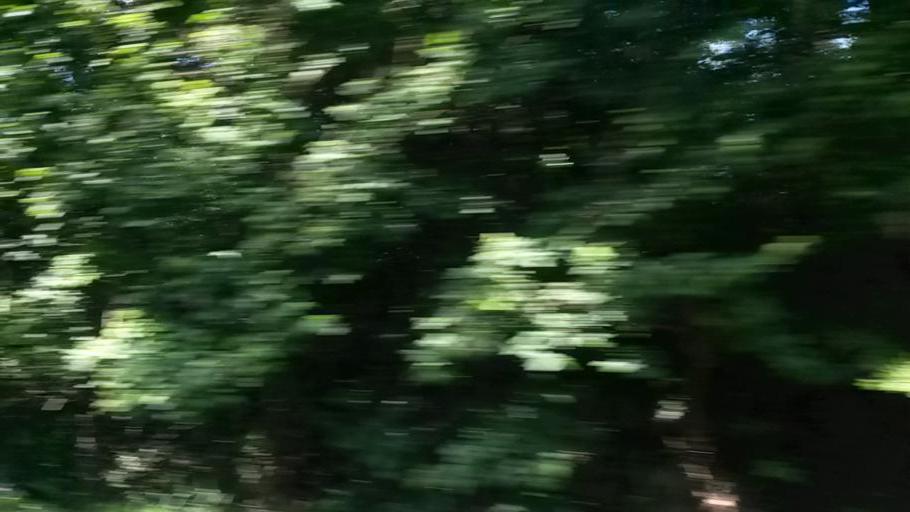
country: IE
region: Leinster
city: Donabate
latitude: 53.4926
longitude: -6.1835
